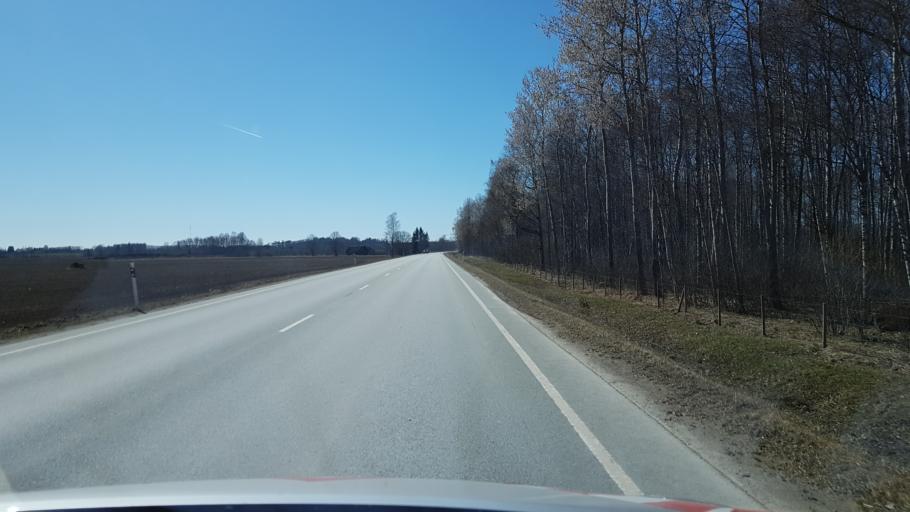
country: EE
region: Laeaene-Virumaa
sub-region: Someru vald
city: Someru
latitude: 59.4415
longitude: 26.3938
